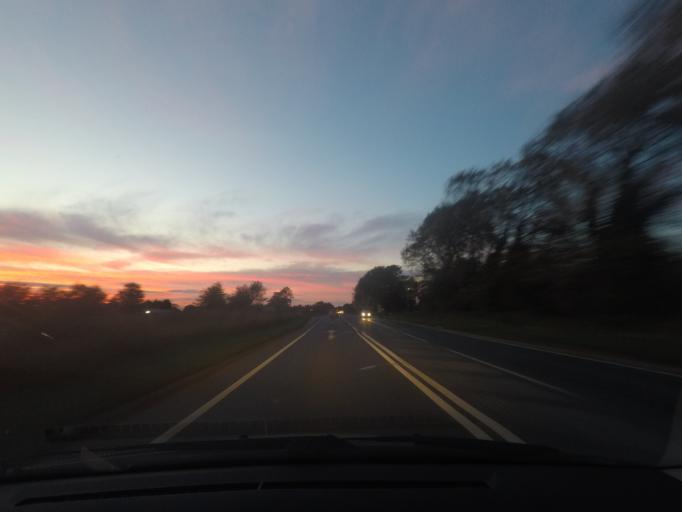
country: GB
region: England
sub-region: East Riding of Yorkshire
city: Pocklington
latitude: 53.9245
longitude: -0.8077
